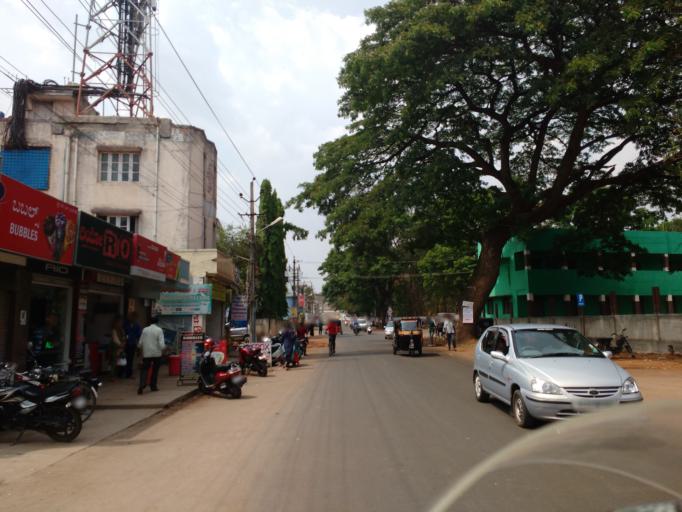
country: IN
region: Karnataka
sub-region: Hassan
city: Hassan
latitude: 13.0071
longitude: 76.1024
